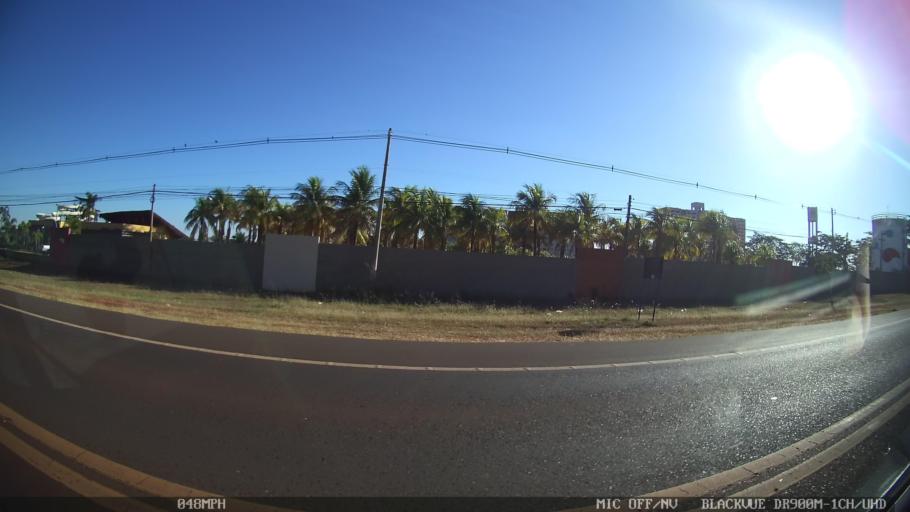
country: BR
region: Sao Paulo
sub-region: Olimpia
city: Olimpia
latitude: -20.7157
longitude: -48.9080
